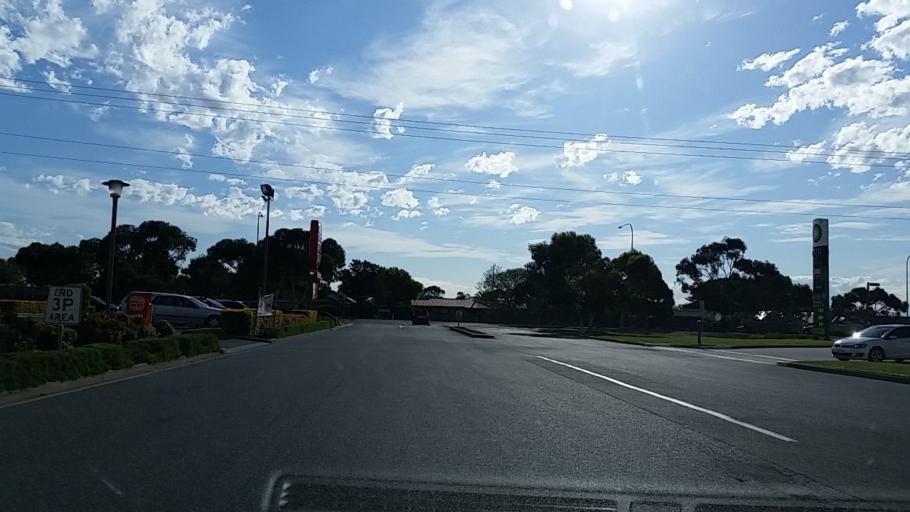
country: AU
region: South Australia
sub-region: Onkaparinga
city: Seaford
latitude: -35.1890
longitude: 138.4784
